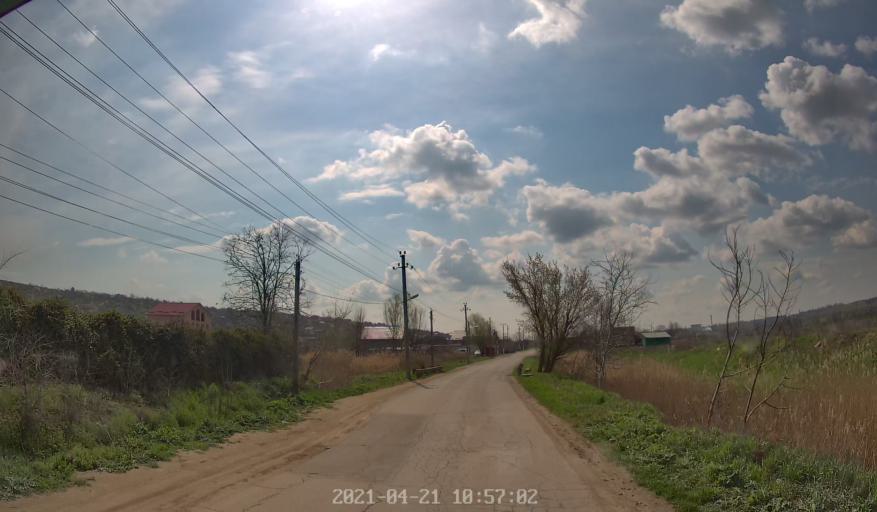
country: MD
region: Chisinau
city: Singera
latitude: 46.9620
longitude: 28.9378
